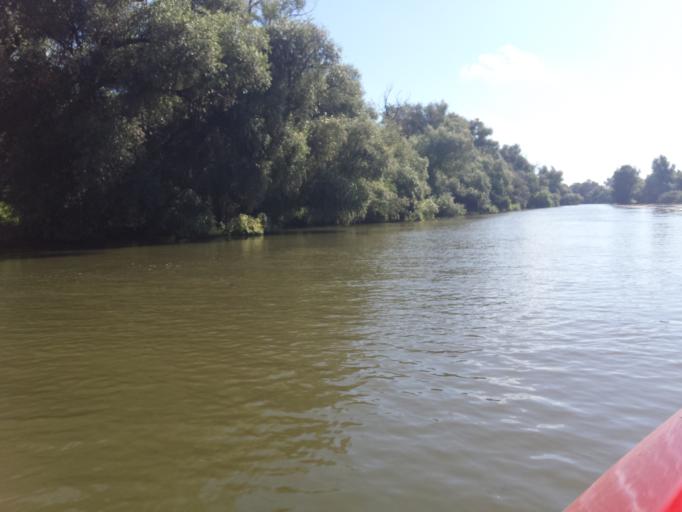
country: RO
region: Tulcea
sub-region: Comuna Mahmudia
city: Mahmudia
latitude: 45.2163
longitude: 29.1758
